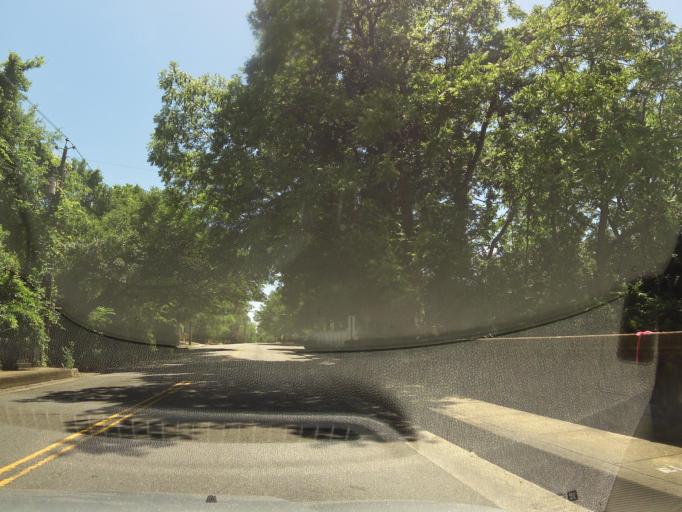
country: US
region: South Carolina
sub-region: Aiken County
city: Aiken
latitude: 33.5574
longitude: -81.7210
